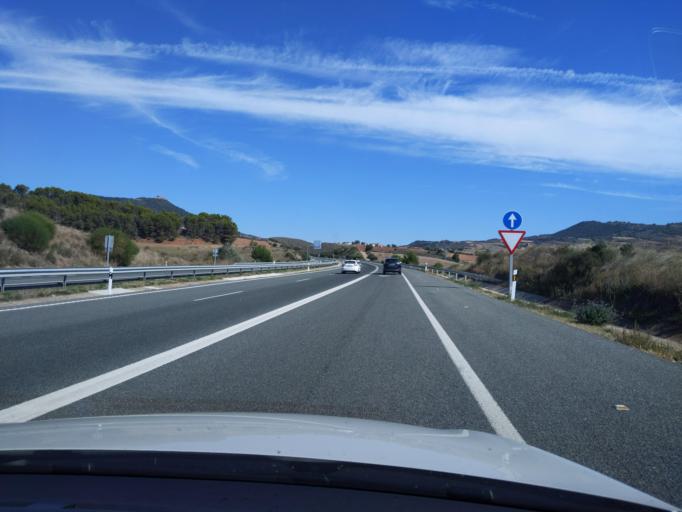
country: ES
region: Navarre
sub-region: Provincia de Navarra
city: Arroniz
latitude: 42.6020
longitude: -2.1180
